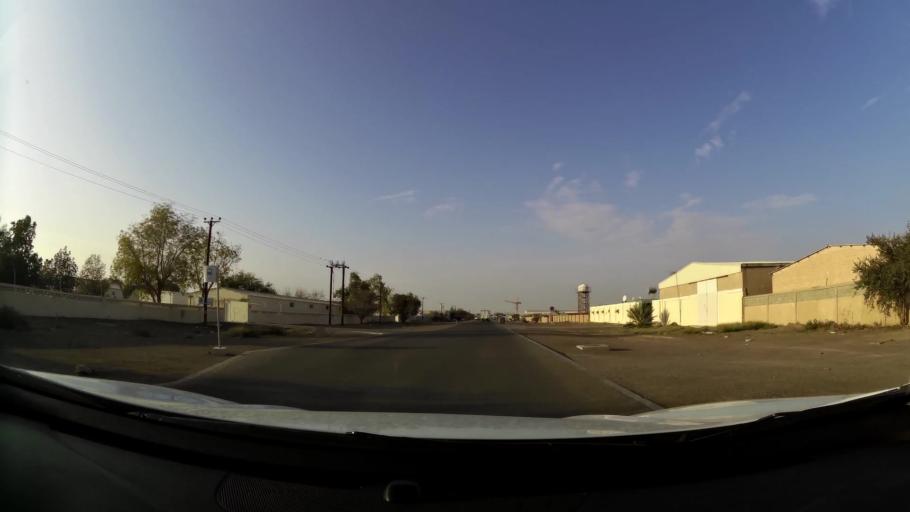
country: AE
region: Abu Dhabi
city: Al Ain
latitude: 24.1461
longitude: 55.8259
